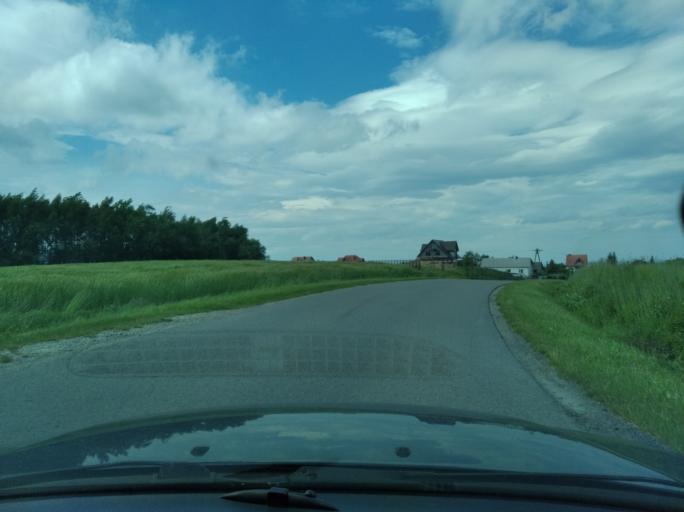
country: PL
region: Subcarpathian Voivodeship
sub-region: Powiat ropczycko-sedziszowski
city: Ropczyce
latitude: 50.0218
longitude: 21.6053
